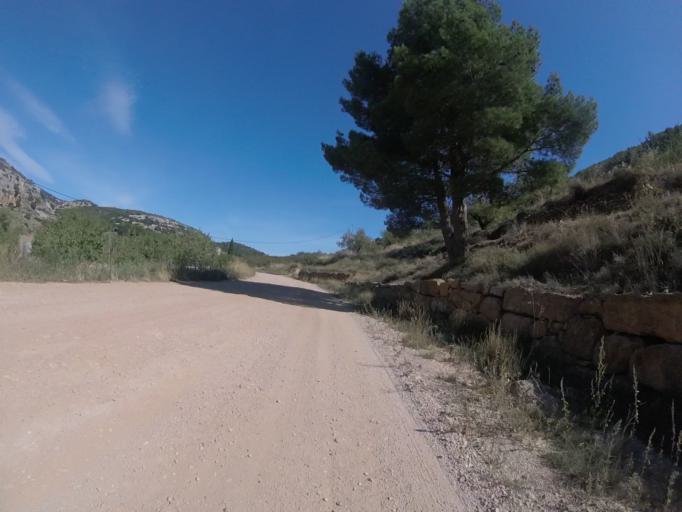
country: ES
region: Valencia
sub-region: Provincia de Castello
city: Sierra-Engarceran
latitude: 40.2706
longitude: -0.0129
